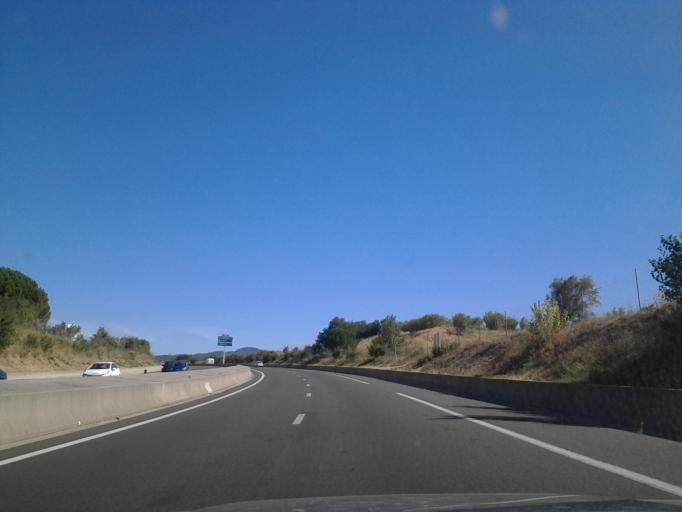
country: FR
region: Languedoc-Roussillon
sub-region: Departement de l'Herault
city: Nebian
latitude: 43.6468
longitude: 3.4496
